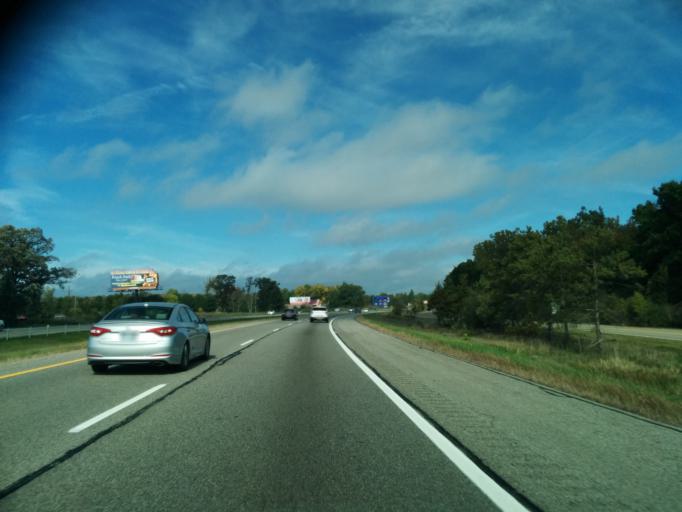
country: US
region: Michigan
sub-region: Livingston County
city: Brighton
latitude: 42.6174
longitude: -83.7474
